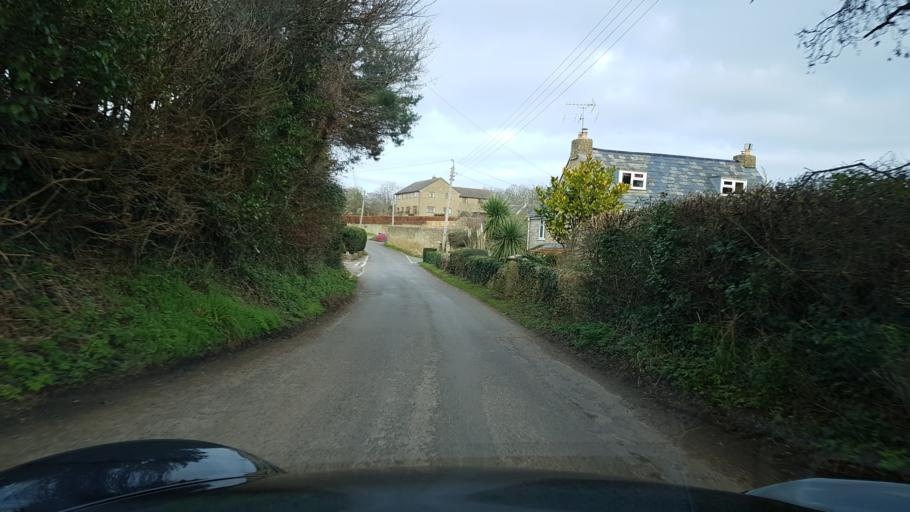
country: GB
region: England
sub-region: Dorset
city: Bridport
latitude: 50.7230
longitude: -2.7164
